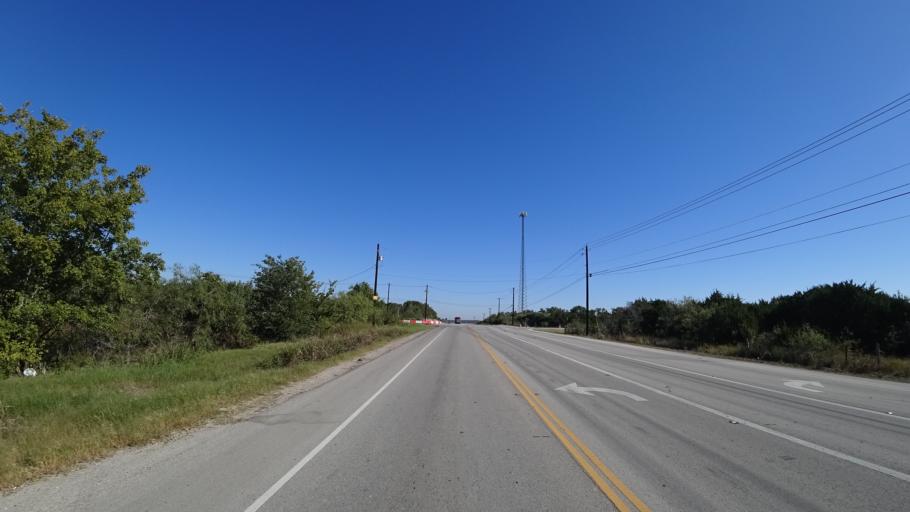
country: US
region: Texas
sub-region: Travis County
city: Hornsby Bend
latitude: 30.2752
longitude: -97.6004
